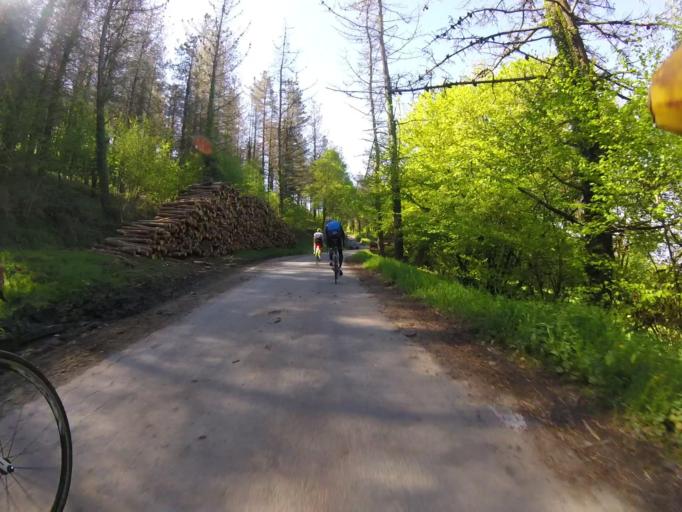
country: ES
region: Basque Country
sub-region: Provincia de Guipuzcoa
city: Errezil
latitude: 43.1966
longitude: -2.2005
